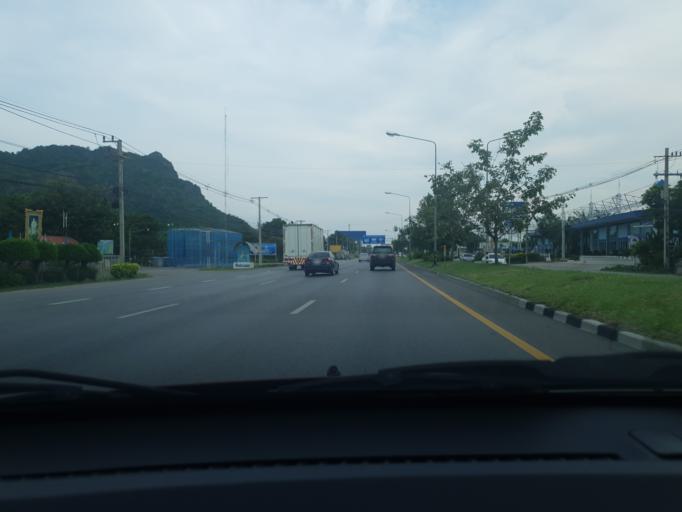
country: TH
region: Phetchaburi
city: Cha-am
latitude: 12.8295
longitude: 99.9353
